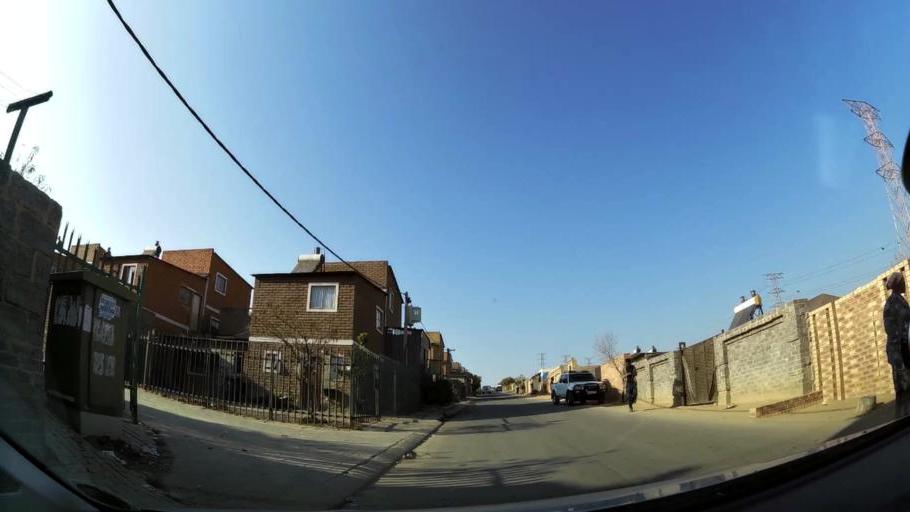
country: ZA
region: Gauteng
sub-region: City of Johannesburg Metropolitan Municipality
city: Modderfontein
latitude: -26.0961
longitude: 28.1091
